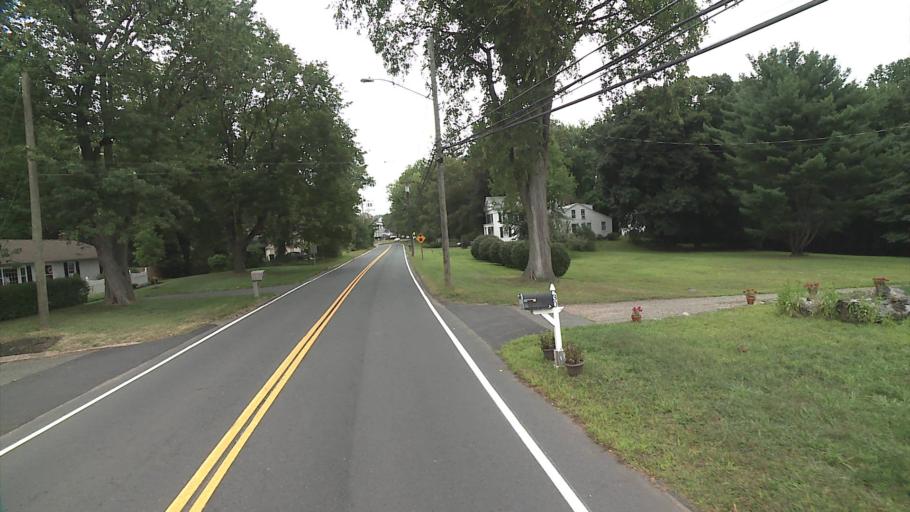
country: US
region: Connecticut
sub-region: Tolland County
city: Rockville
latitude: 41.8357
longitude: -72.4676
